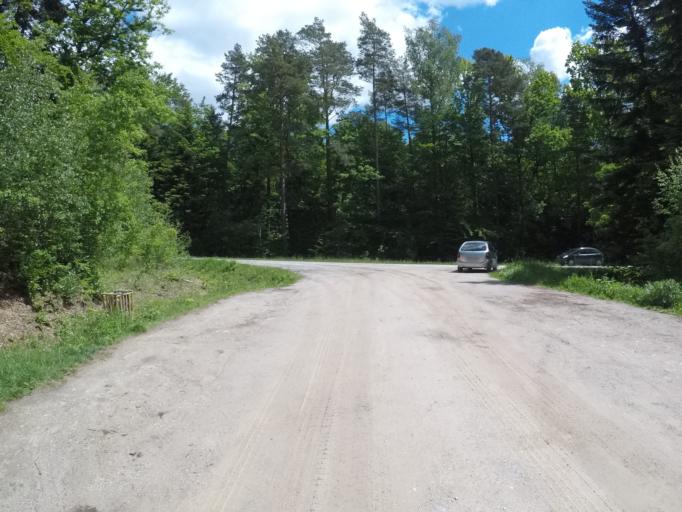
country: PL
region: Swietokrzyskie
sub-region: Powiat kielecki
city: Zagnansk
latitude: 50.9323
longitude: 20.6477
